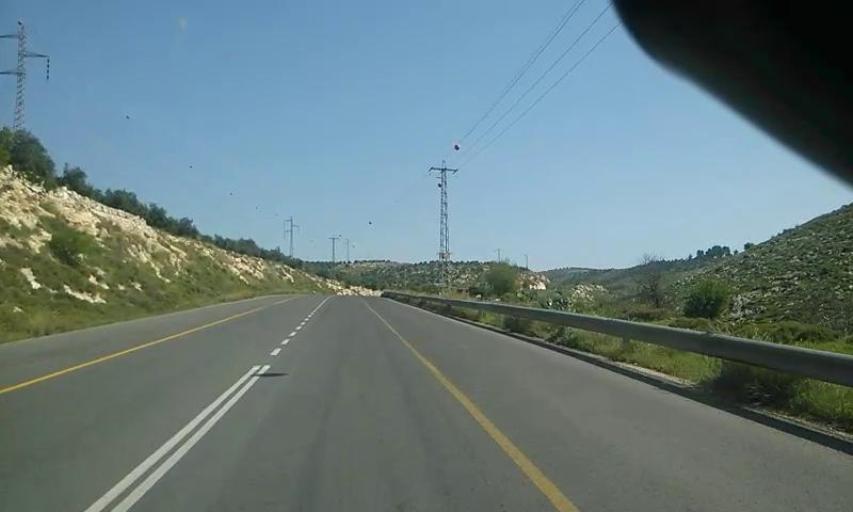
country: PS
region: West Bank
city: Idhna
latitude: 31.5665
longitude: 34.9898
